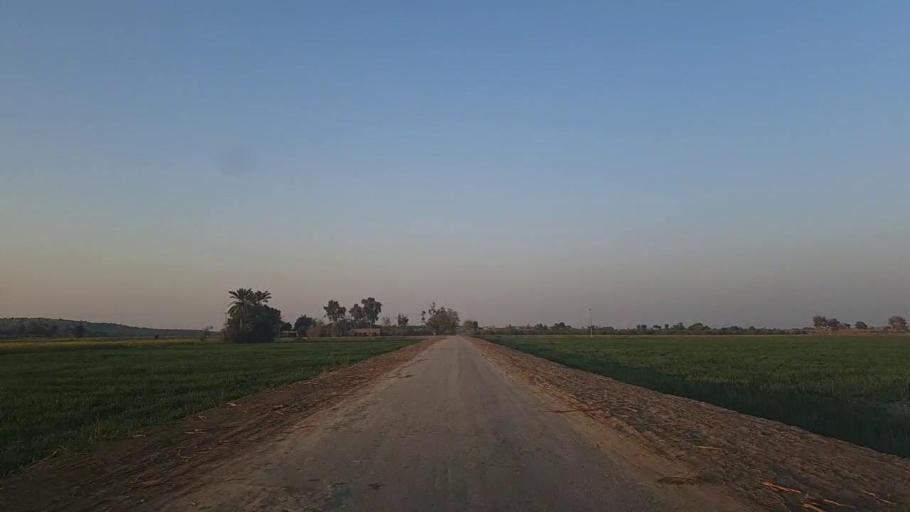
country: PK
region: Sindh
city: Jam Sahib
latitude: 26.3500
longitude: 68.7147
